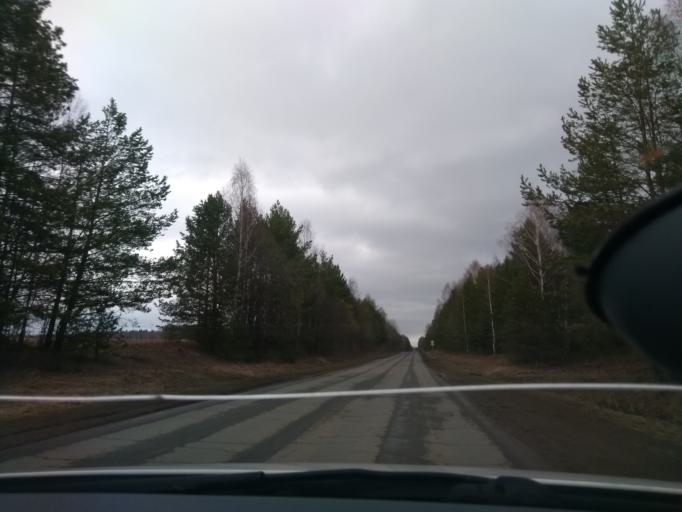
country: RU
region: Perm
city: Kungur
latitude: 57.3509
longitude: 56.7997
